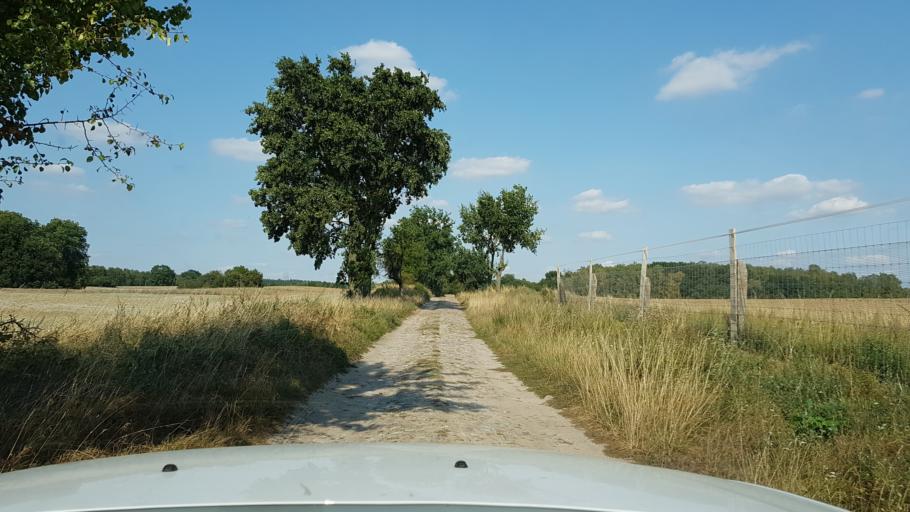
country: PL
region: West Pomeranian Voivodeship
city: Trzcinsko Zdroj
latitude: 52.8969
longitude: 14.5526
